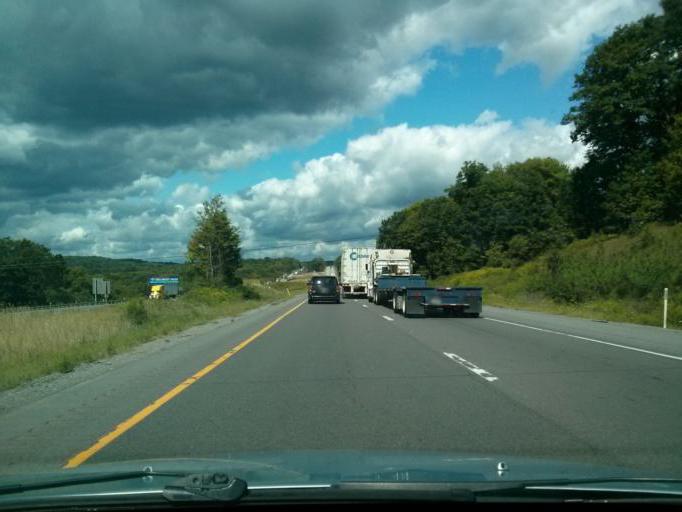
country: US
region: Pennsylvania
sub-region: Jefferson County
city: Falls Creek
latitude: 41.1482
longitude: -78.7925
